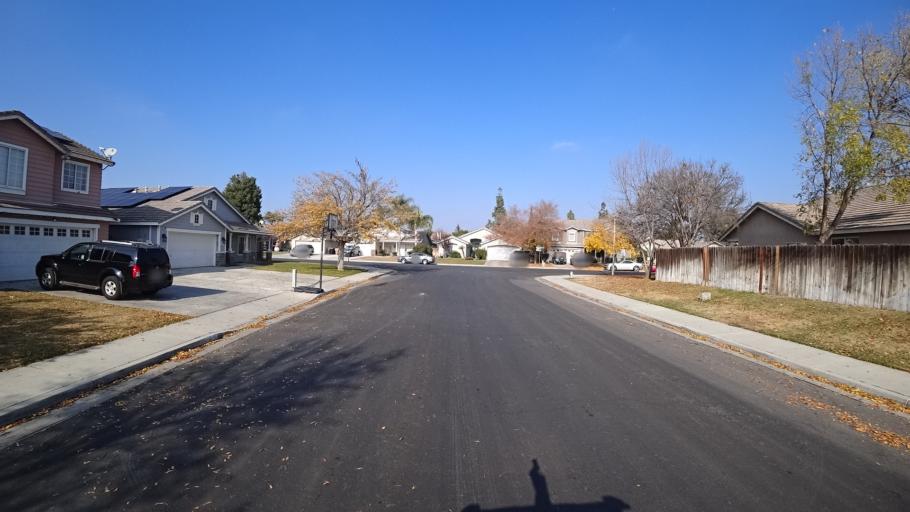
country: US
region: California
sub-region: Kern County
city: Greenacres
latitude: 35.3075
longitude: -119.0837
